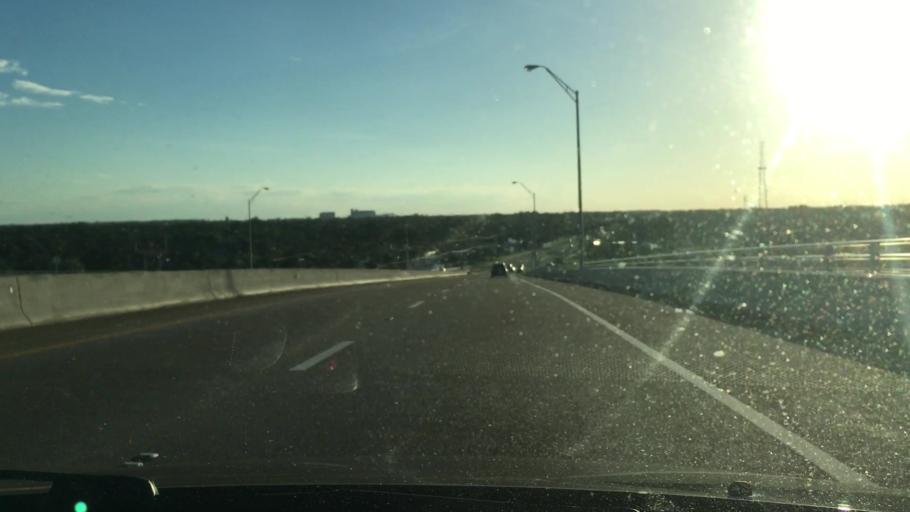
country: US
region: Florida
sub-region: Volusia County
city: Holly Hill
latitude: 29.2304
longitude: -81.0239
